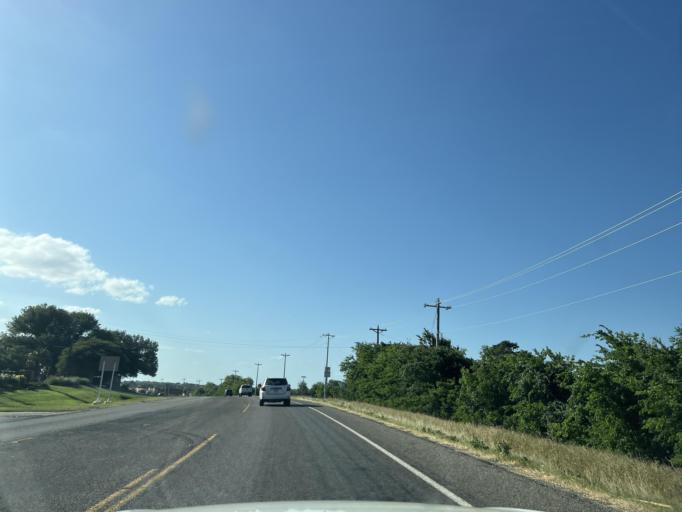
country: US
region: Texas
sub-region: Washington County
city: Brenham
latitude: 30.1744
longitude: -96.3818
